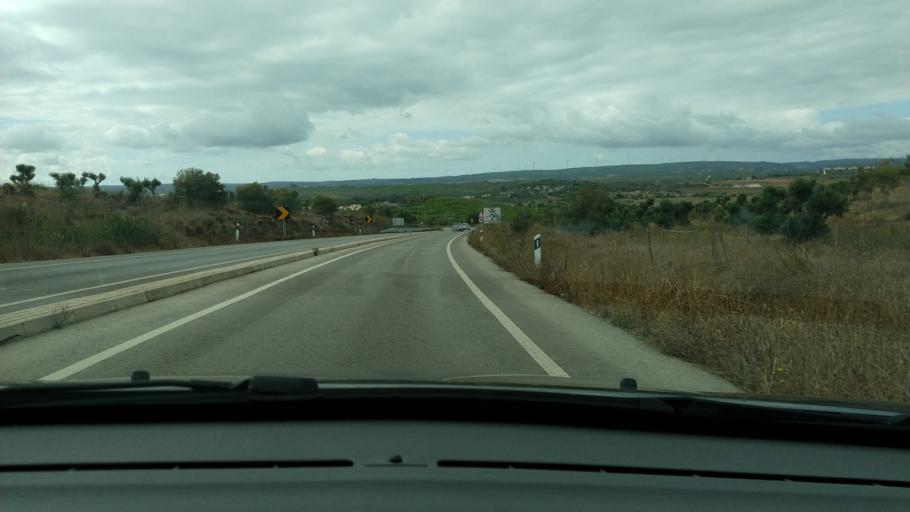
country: PT
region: Faro
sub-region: Lagos
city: Lagos
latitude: 37.0980
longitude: -8.7439
